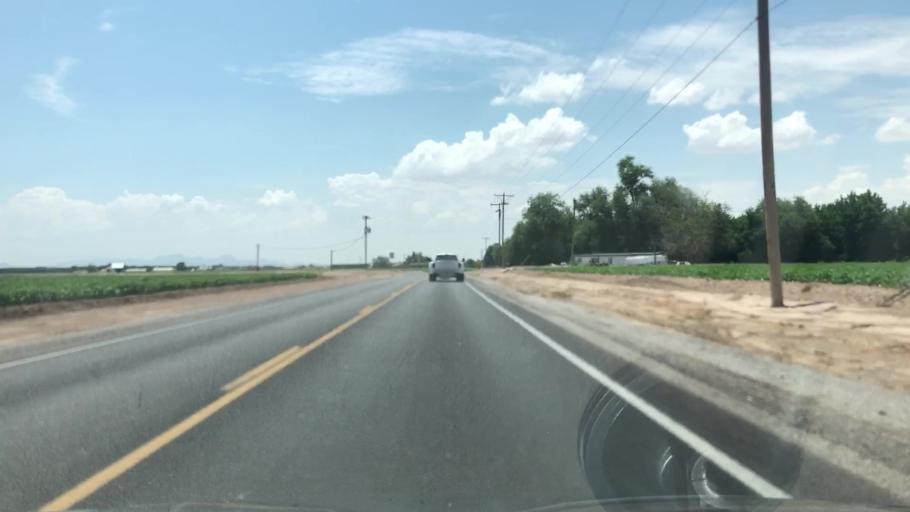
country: US
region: New Mexico
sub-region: Dona Ana County
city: La Union
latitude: 31.9754
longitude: -106.6516
